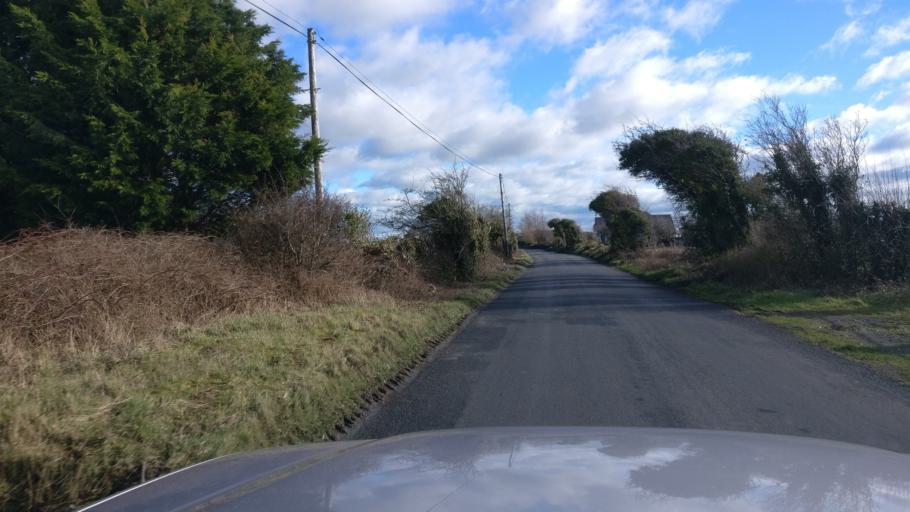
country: IE
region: Connaught
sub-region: County Galway
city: Oranmore
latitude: 53.2731
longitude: -8.8834
